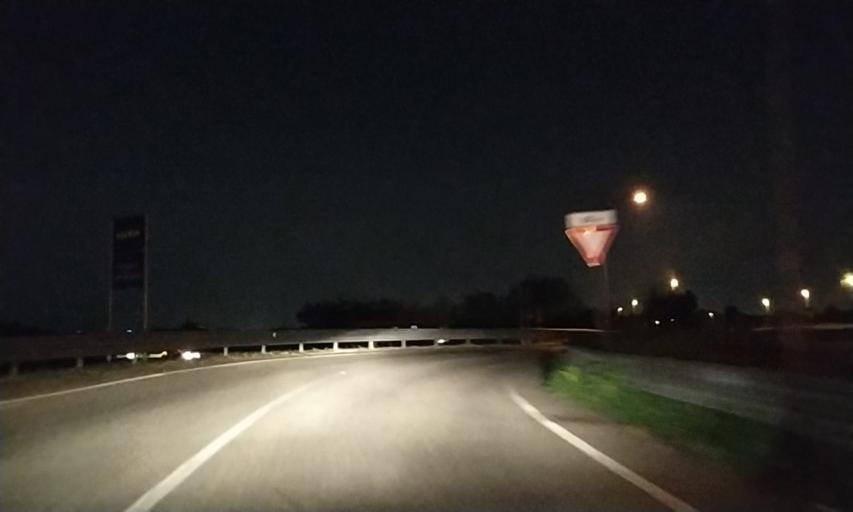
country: IT
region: Piedmont
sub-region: Provincia di Torino
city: Collegno
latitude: 45.0969
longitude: 7.5793
